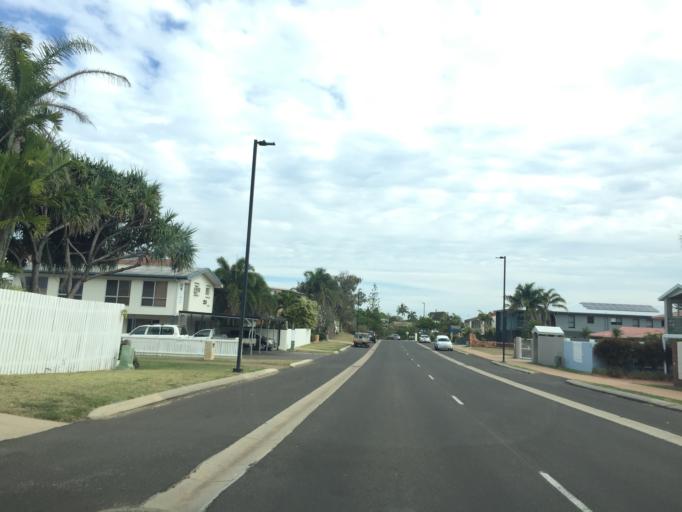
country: AU
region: Queensland
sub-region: Bundaberg
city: Bundaberg
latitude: -24.8238
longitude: 152.4652
